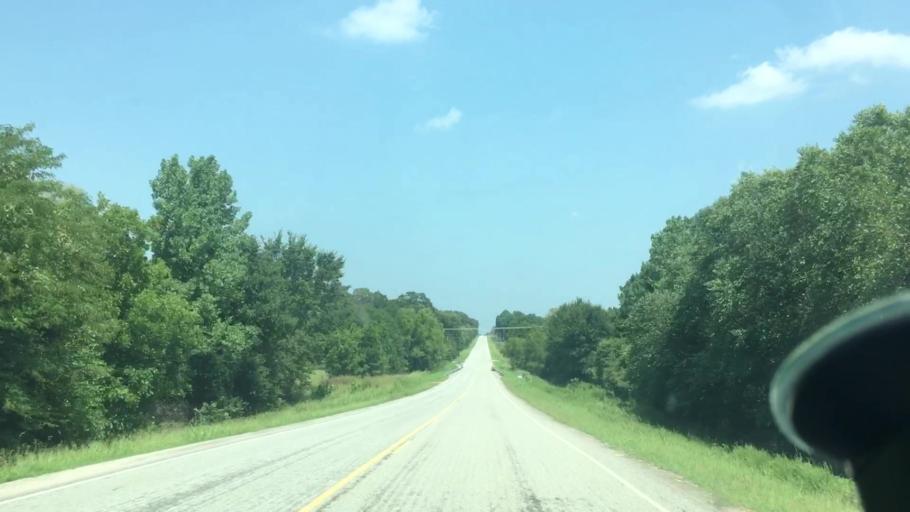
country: US
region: Oklahoma
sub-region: Atoka County
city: Atoka
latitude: 34.2555
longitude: -95.9361
